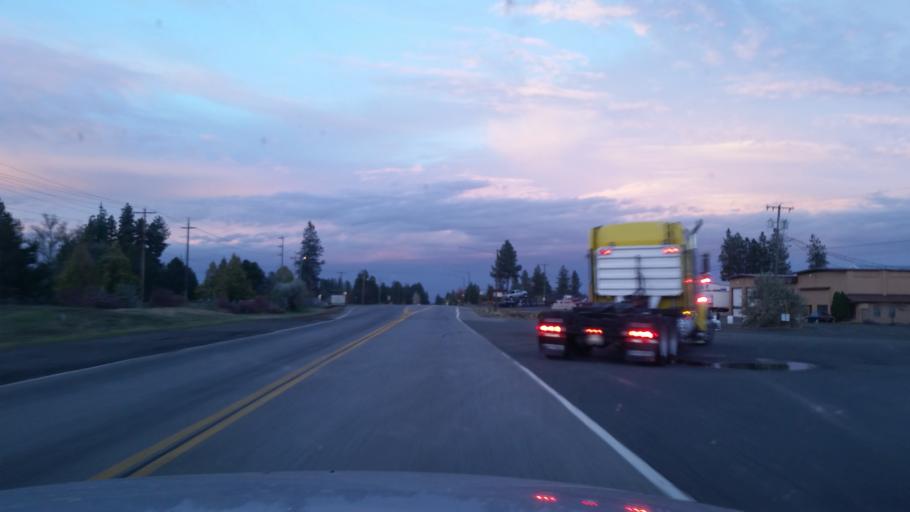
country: US
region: Washington
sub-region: Spokane County
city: Spokane
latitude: 47.6264
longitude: -117.5017
